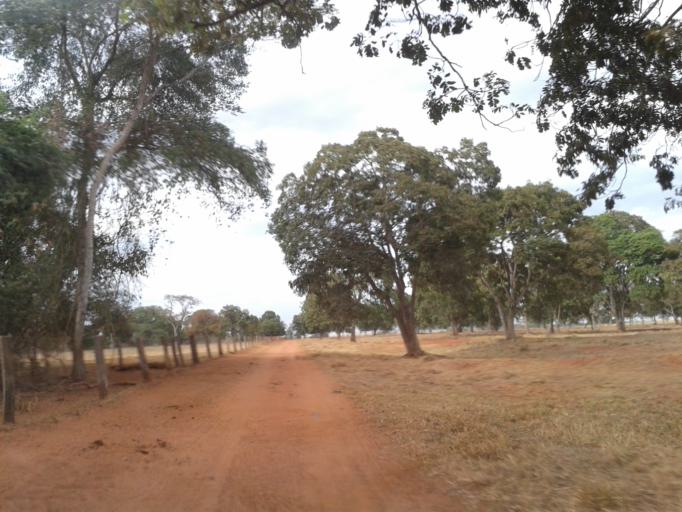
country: BR
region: Minas Gerais
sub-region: Santa Vitoria
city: Santa Vitoria
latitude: -18.7531
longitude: -50.1953
